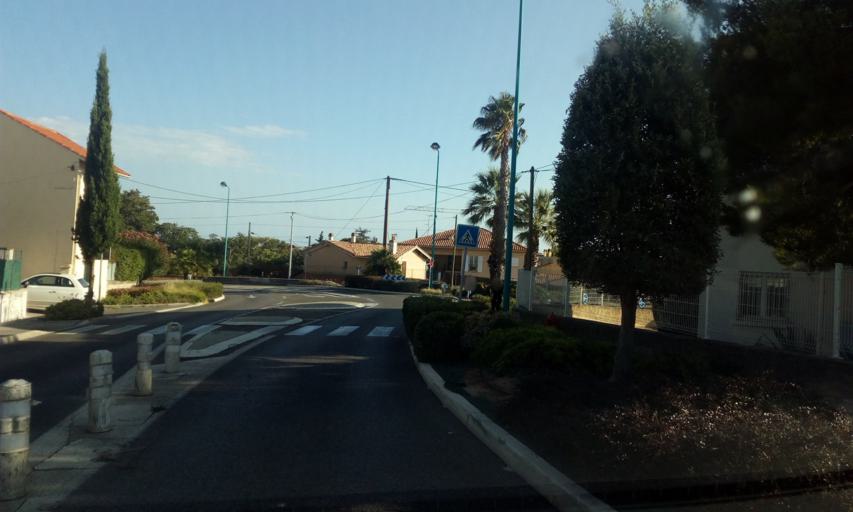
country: FR
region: Provence-Alpes-Cote d'Azur
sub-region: Departement du Var
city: Bandol
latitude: 43.1415
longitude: 5.7481
